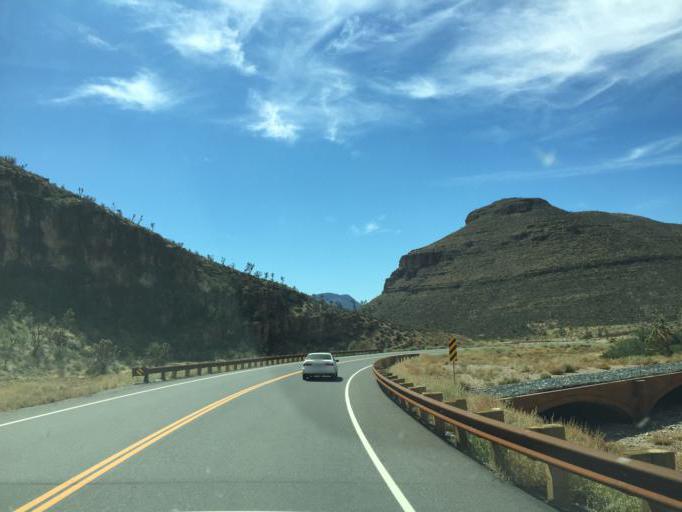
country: US
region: Arizona
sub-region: Mohave County
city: Meadview
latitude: 35.8986
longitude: -113.9433
